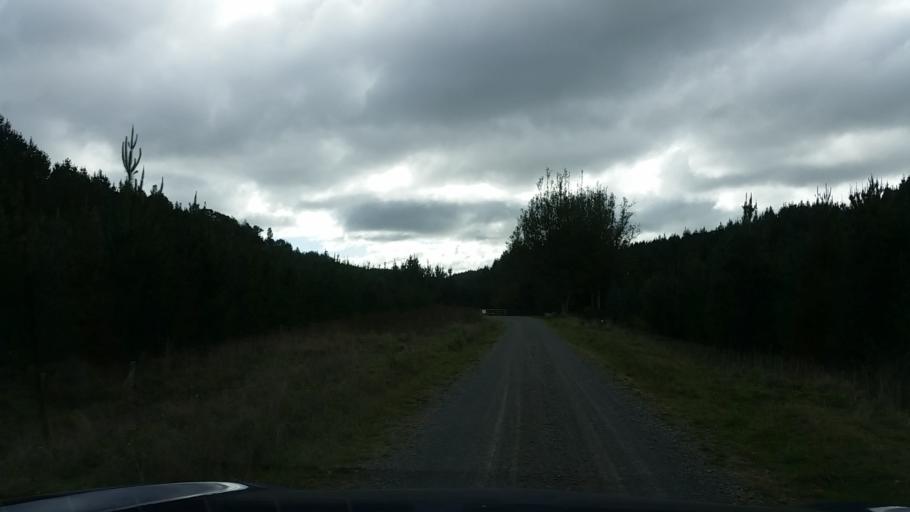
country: NZ
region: Bay of Plenty
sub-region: Western Bay of Plenty District
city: Maketu
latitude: -37.9684
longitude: 176.4092
